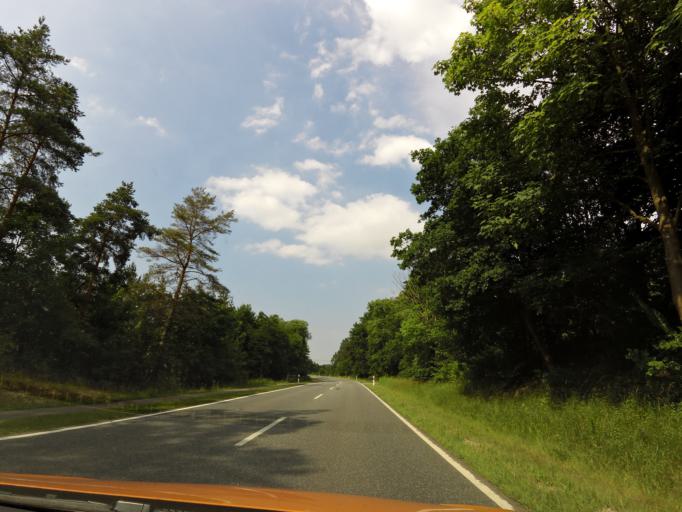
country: DE
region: Mecklenburg-Vorpommern
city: Krakow am See
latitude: 53.6747
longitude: 12.2686
